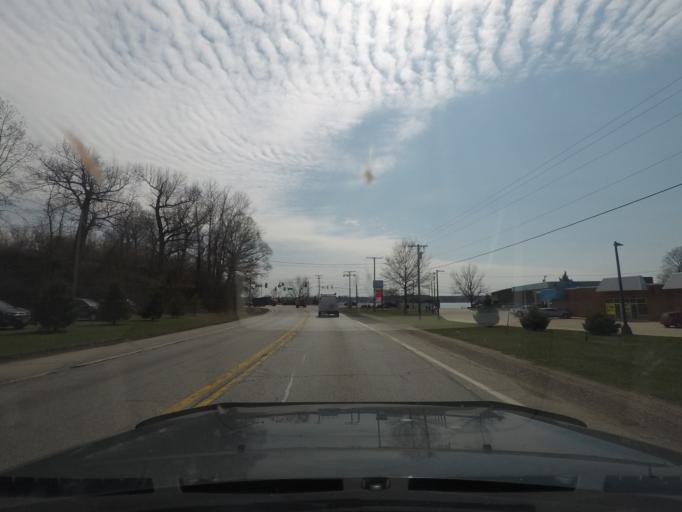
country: US
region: Indiana
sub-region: LaPorte County
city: LaPorte
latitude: 41.6401
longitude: -86.7469
